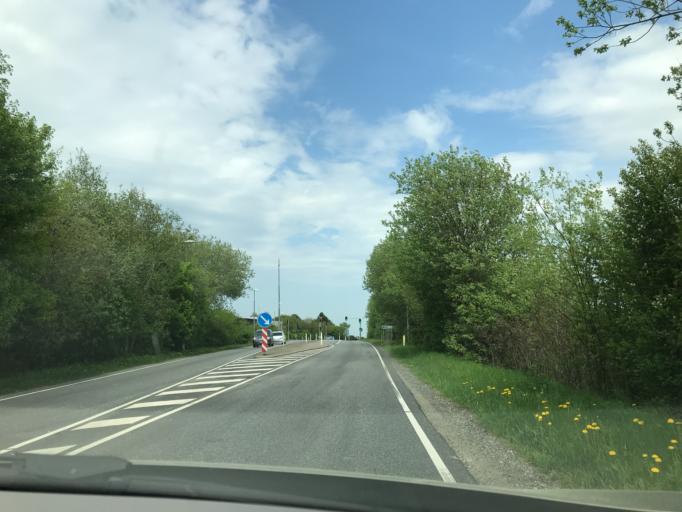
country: DK
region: South Denmark
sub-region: Assens Kommune
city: Assens
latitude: 55.2802
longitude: 9.9206
